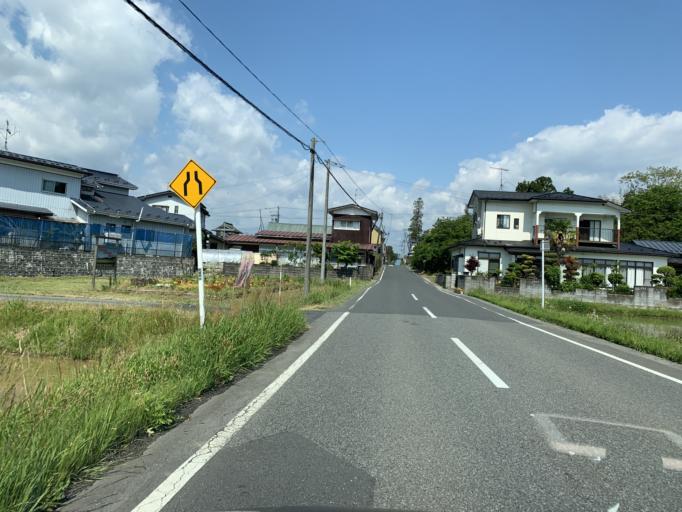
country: JP
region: Iwate
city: Ichinoseki
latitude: 38.7957
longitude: 141.0248
